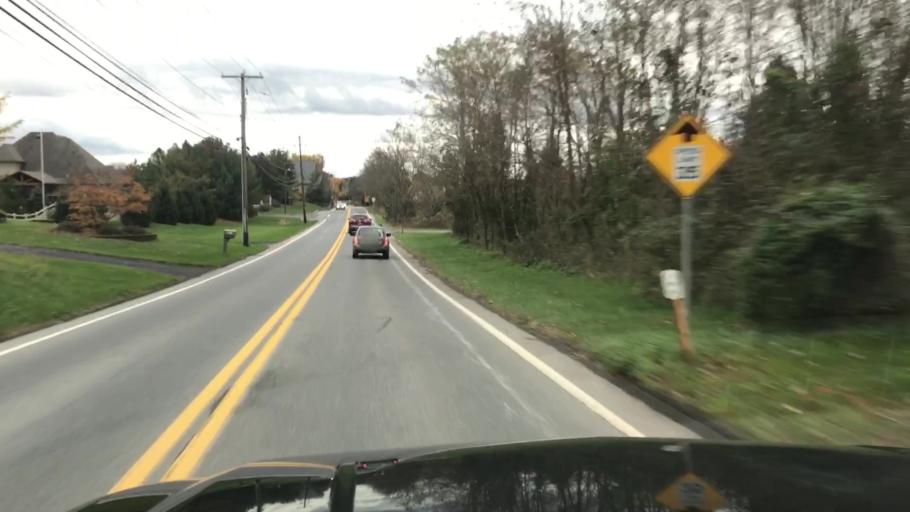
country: US
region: Pennsylvania
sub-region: Cumberland County
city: Shiremanstown
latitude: 40.1705
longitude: -76.9272
